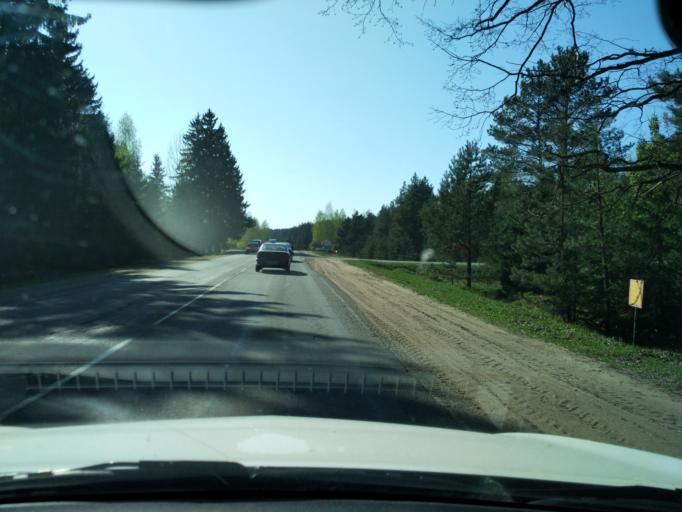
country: BY
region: Minsk
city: Lyeskawka
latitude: 53.9606
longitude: 27.7117
